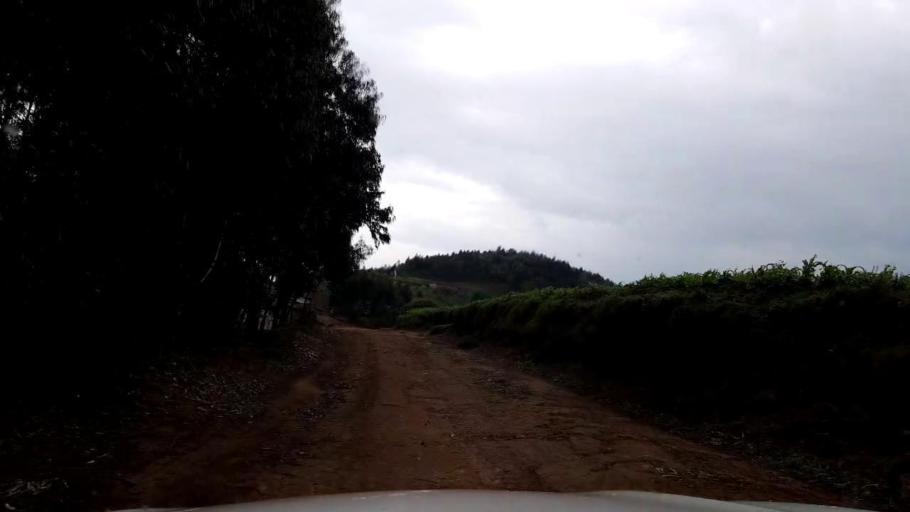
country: RW
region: Western Province
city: Kibuye
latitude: -2.0173
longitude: 29.4654
